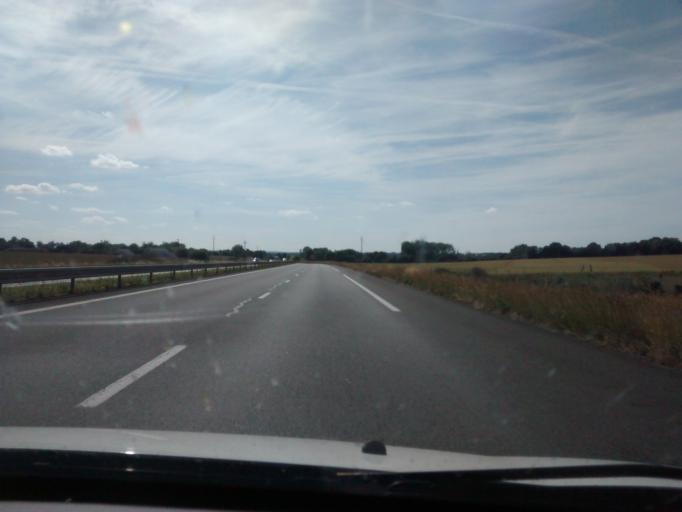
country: FR
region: Pays de la Loire
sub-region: Departement de la Mayenne
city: Soulge-sur-Ouette
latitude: 48.0748
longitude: -0.6037
